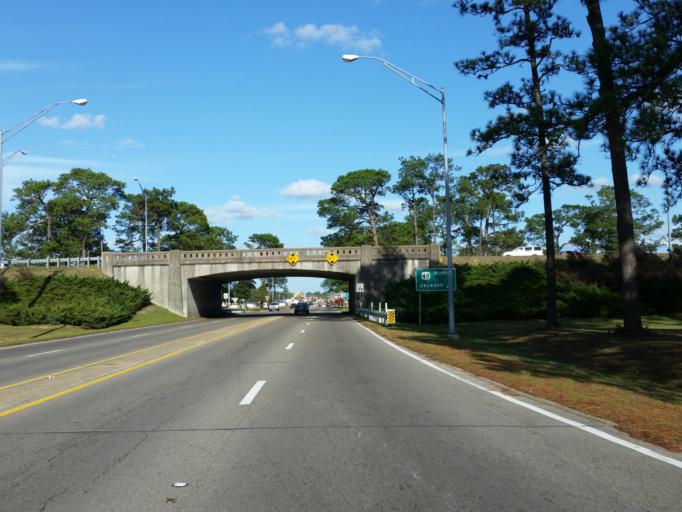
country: US
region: Mississippi
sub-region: Forrest County
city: Hattiesburg
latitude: 31.3068
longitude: -89.3171
